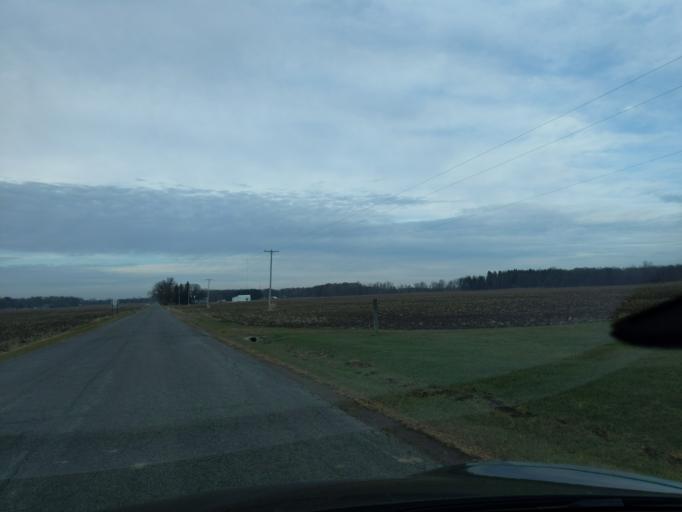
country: US
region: Michigan
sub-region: Ingham County
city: Okemos
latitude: 42.6553
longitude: -84.3836
